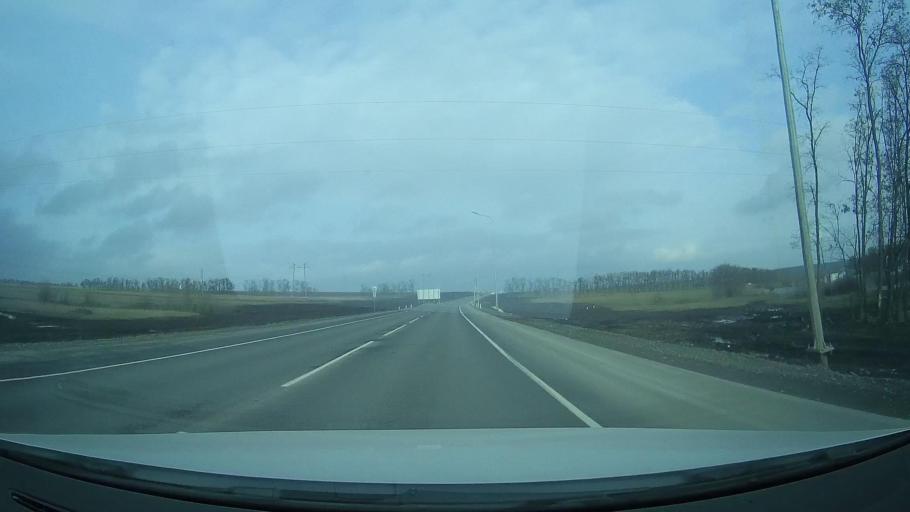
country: RU
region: Rostov
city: Grushevskaya
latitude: 47.3841
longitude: 39.8455
